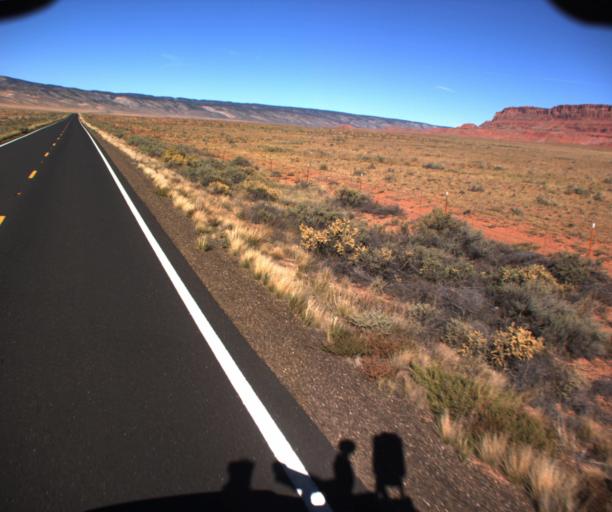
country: US
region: Arizona
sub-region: Coconino County
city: Page
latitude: 36.7110
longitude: -111.9731
